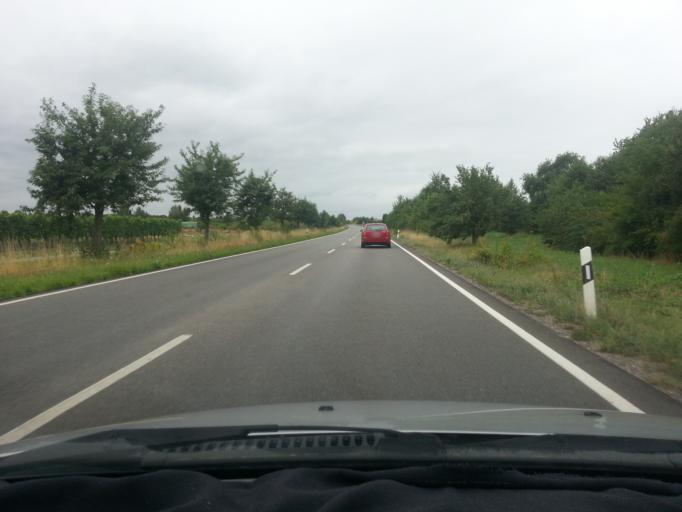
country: DE
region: Rheinland-Pfalz
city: Niederkirchen bei Deidesheim
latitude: 49.4214
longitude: 8.2010
